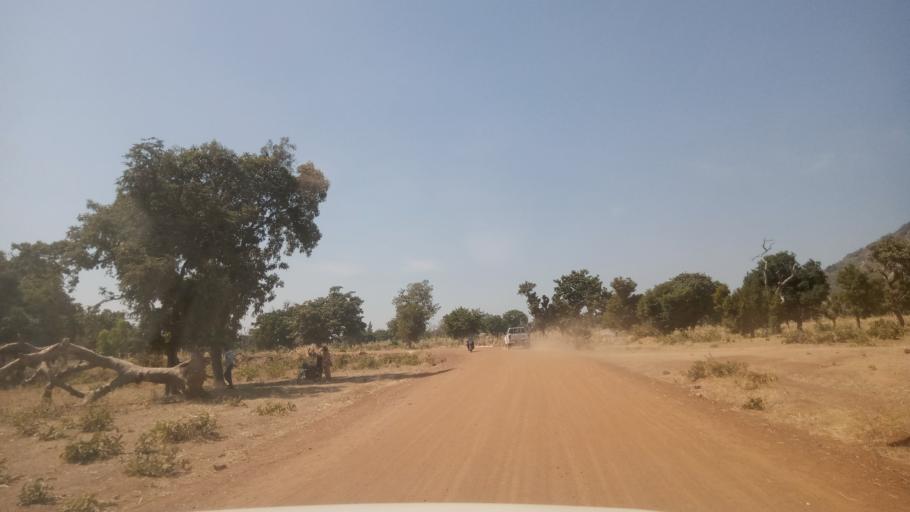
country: NG
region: Borno
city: Uba
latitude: 10.4280
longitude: 12.9965
